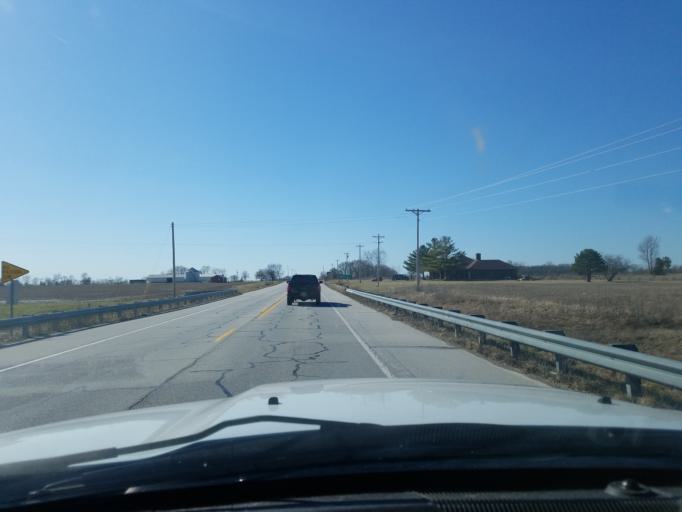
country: US
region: Indiana
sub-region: Shelby County
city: Shelbyville
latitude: 39.4960
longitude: -85.8904
